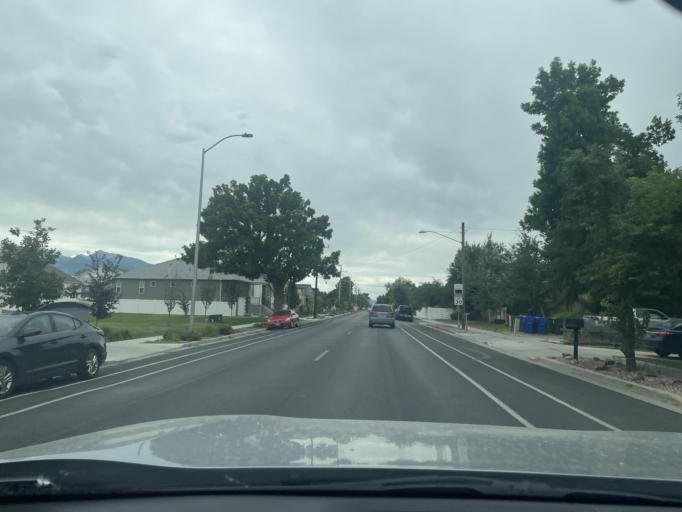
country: US
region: Utah
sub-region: Salt Lake County
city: Millcreek
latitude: 40.6974
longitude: -111.8770
